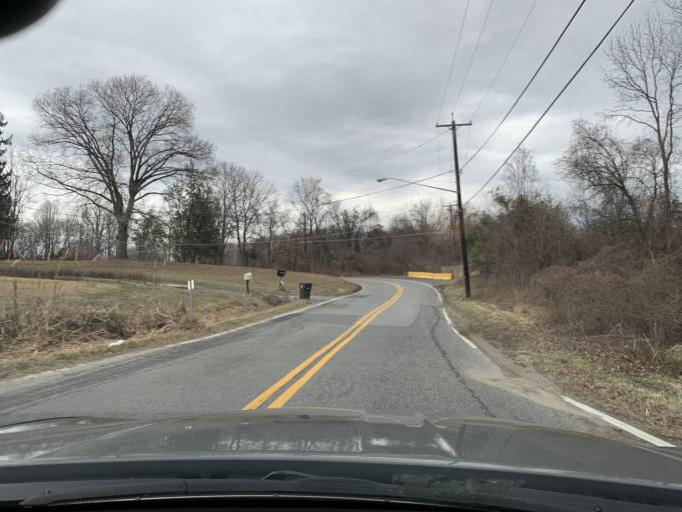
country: US
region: Maryland
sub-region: Prince George's County
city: Walker Mill
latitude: 38.8736
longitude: -76.9017
